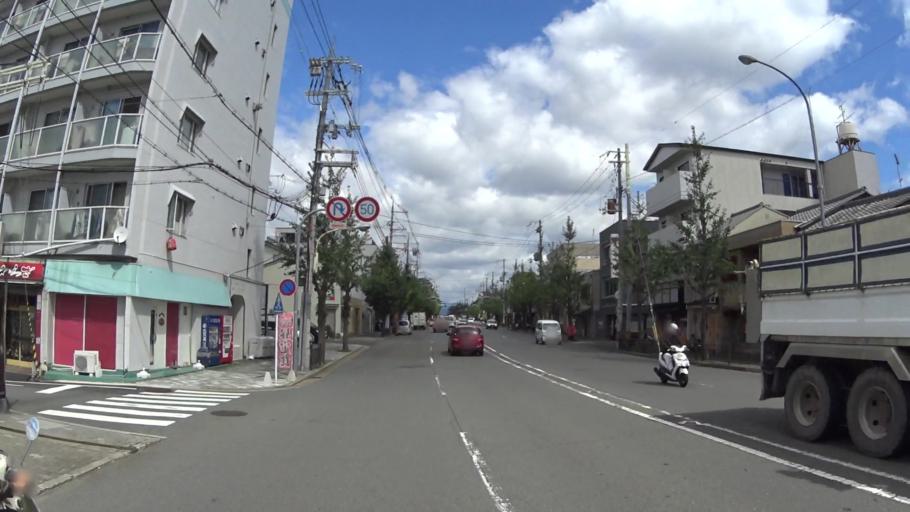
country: JP
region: Kyoto
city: Kyoto
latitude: 34.9857
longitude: 135.7740
